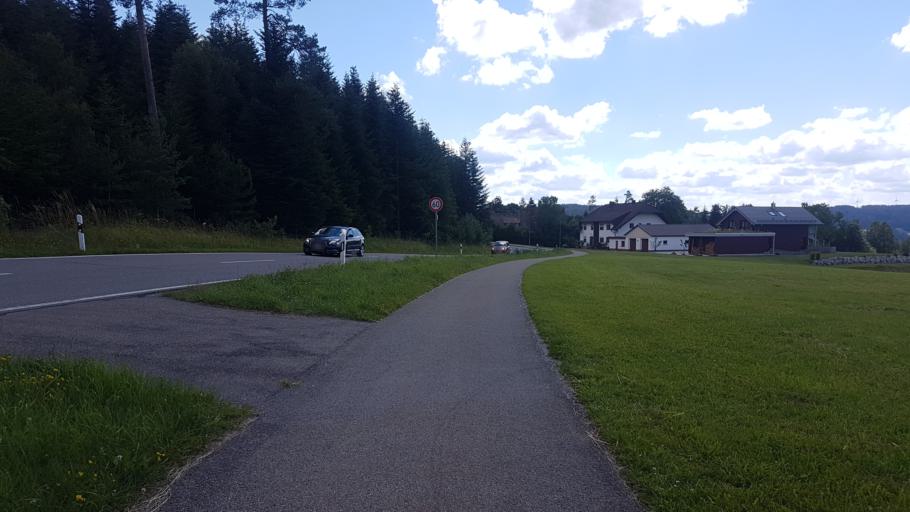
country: DE
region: Baden-Wuerttemberg
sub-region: Freiburg Region
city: Hardt
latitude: 48.2123
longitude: 8.4151
